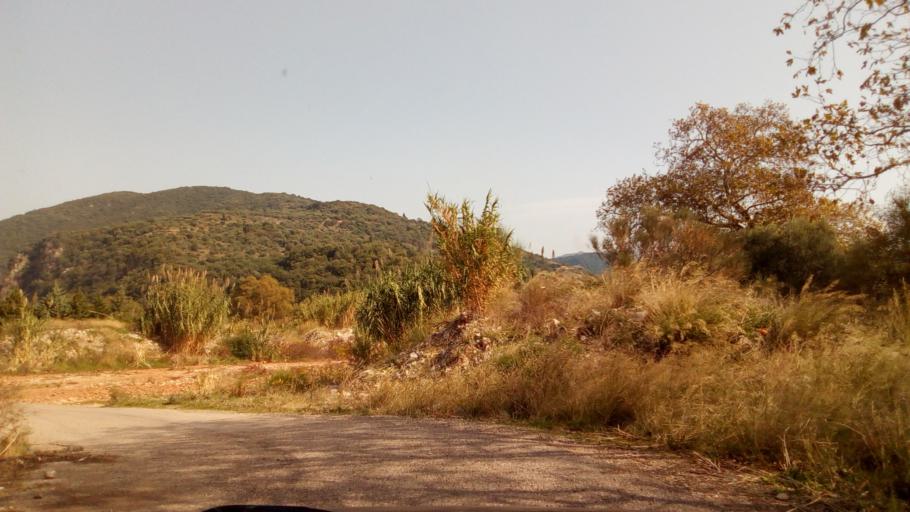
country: GR
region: West Greece
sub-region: Nomos Aitolias kai Akarnanias
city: Nafpaktos
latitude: 38.4159
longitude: 21.8831
